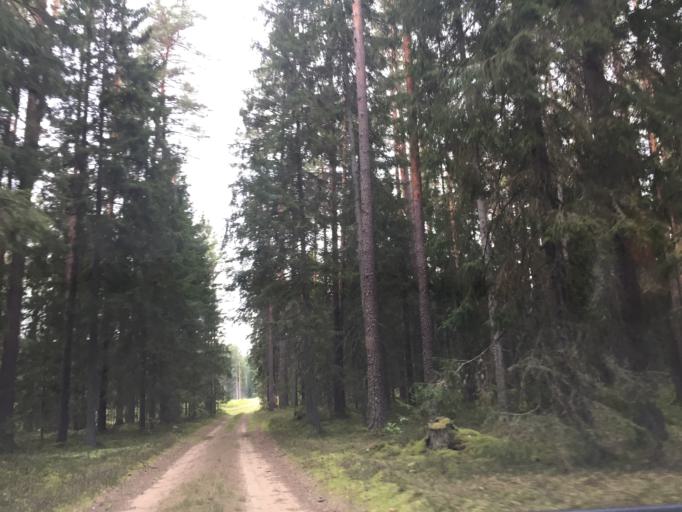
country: LV
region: Baldone
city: Baldone
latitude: 56.7737
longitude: 24.4485
